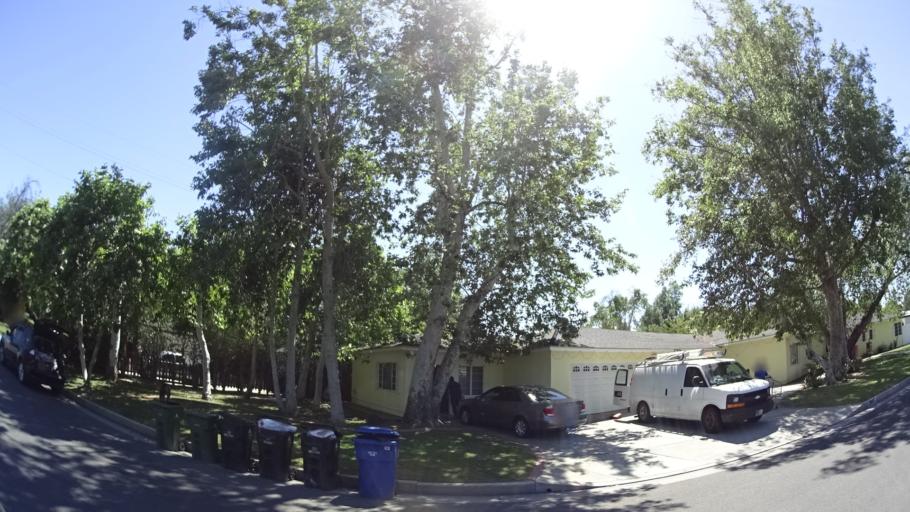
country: US
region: California
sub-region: Los Angeles County
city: Van Nuys
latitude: 34.1759
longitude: -118.4250
